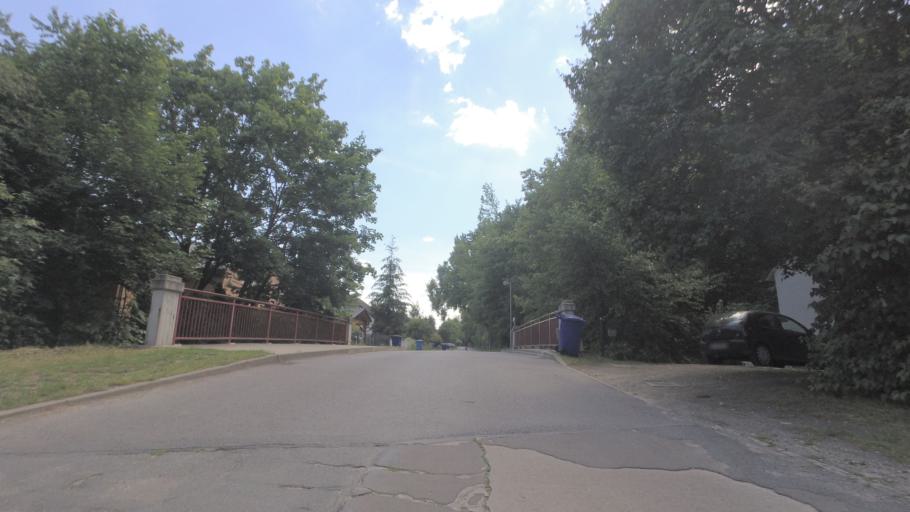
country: DE
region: Brandenburg
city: Rangsdorf
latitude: 52.2846
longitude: 13.4189
